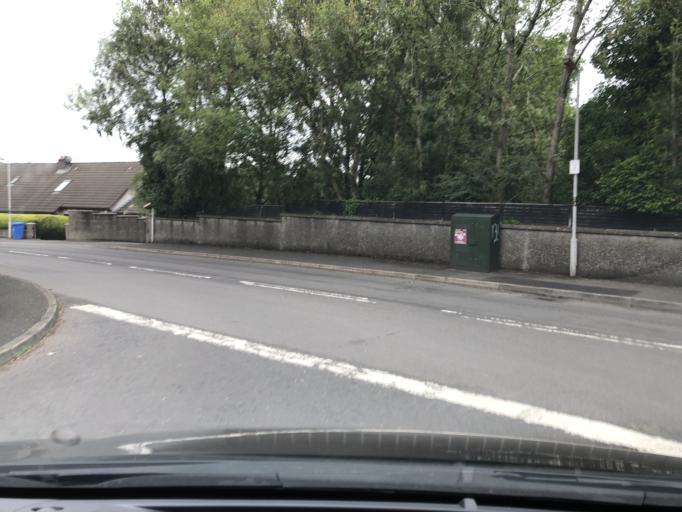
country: GB
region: Northern Ireland
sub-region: Larne District
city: Larne
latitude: 54.8476
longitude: -5.8291
